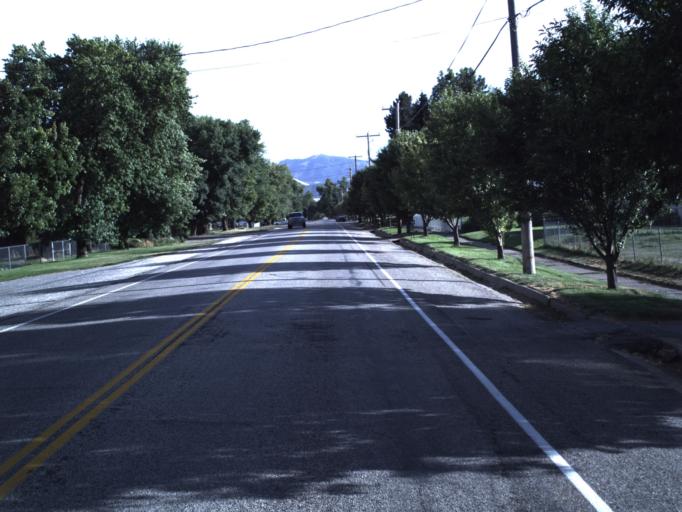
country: US
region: Utah
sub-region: Cache County
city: Wellsville
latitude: 41.6446
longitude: -111.9342
